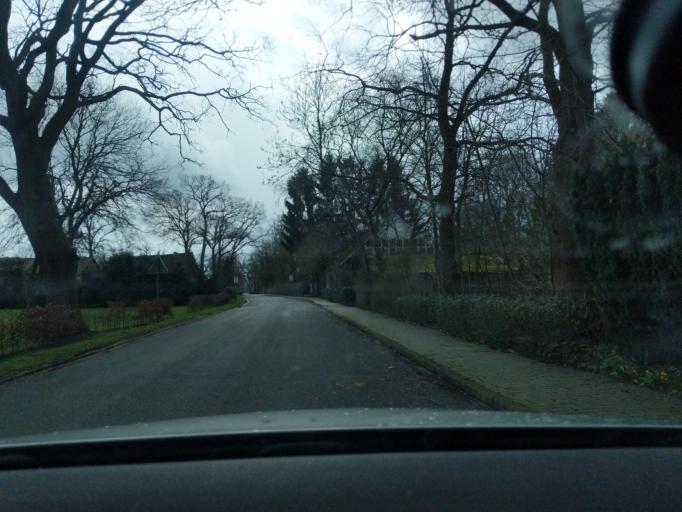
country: DE
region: Lower Saxony
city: Kranenburg
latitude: 53.5966
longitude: 9.1870
